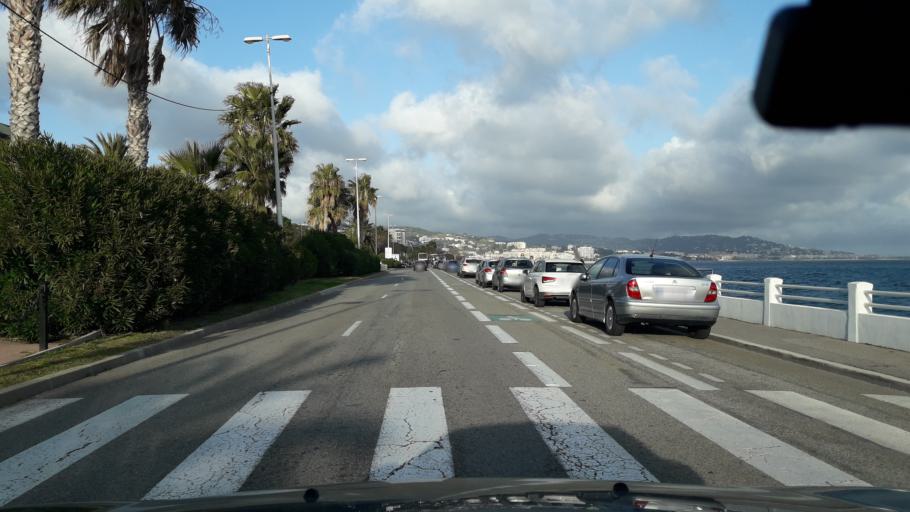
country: FR
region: Provence-Alpes-Cote d'Azur
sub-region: Departement des Alpes-Maritimes
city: Mandelieu-la-Napoule
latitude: 43.5400
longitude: 6.9585
